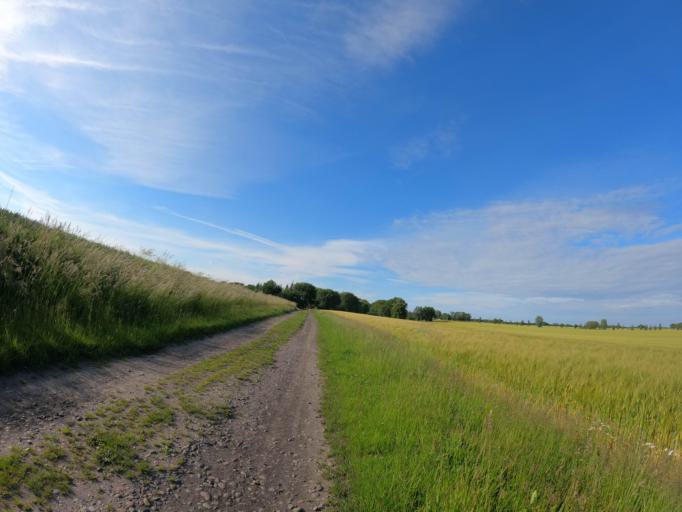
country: DE
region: Mecklenburg-Vorpommern
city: Preetz
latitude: 54.3264
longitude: 12.9738
